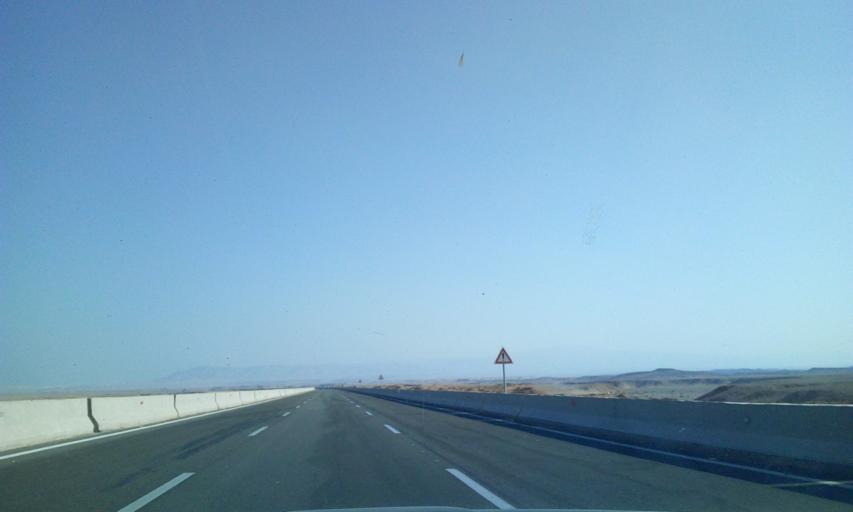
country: EG
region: As Suways
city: Ain Sukhna
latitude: 29.2064
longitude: 32.4937
